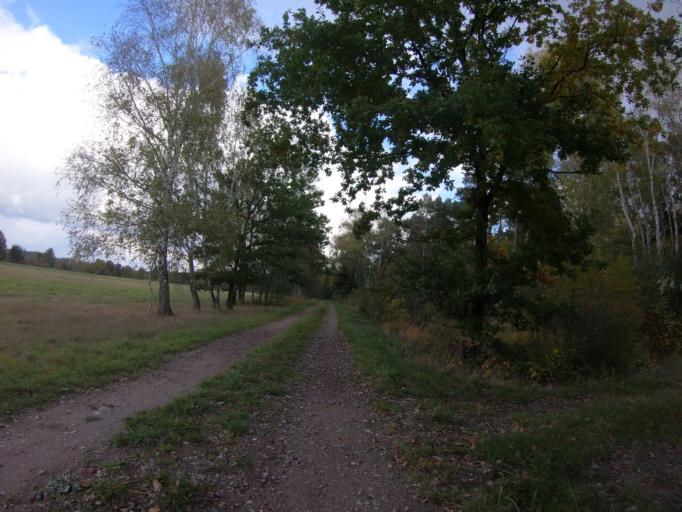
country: DE
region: Lower Saxony
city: Wahrenholz
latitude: 52.5813
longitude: 10.6155
